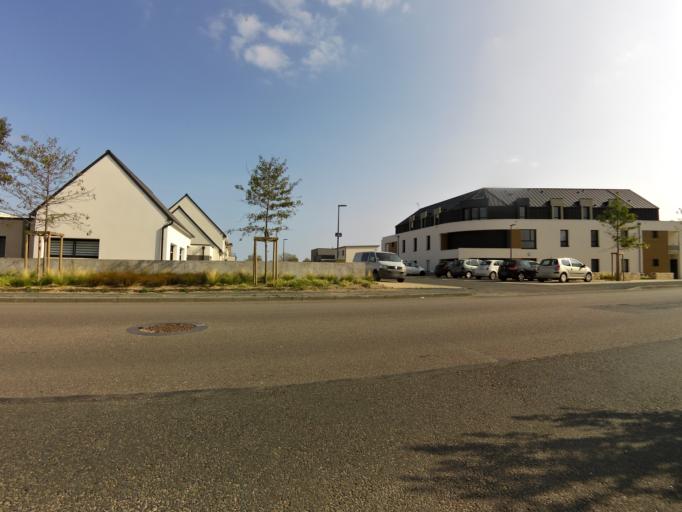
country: FR
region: Brittany
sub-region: Departement du Finistere
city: Loctudy
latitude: 47.8517
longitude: -4.1635
